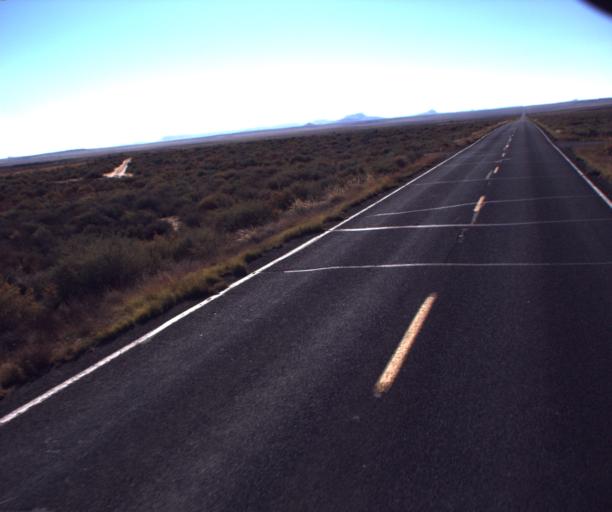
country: US
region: Arizona
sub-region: Navajo County
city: First Mesa
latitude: 35.7206
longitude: -110.5150
